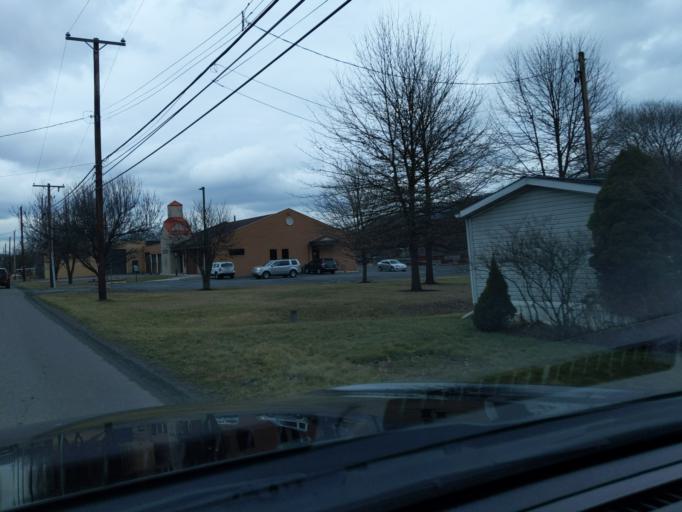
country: US
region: Pennsylvania
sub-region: Blair County
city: Bellwood
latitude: 40.6056
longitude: -78.3323
